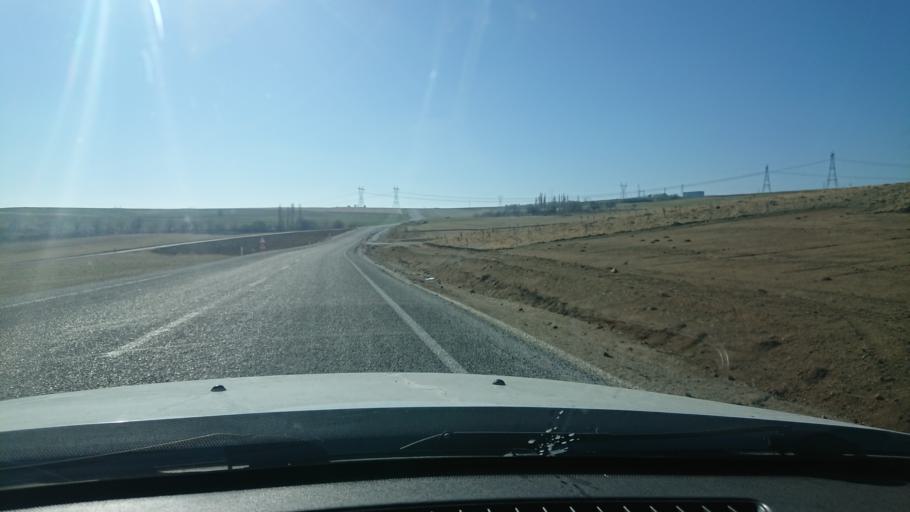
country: TR
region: Aksaray
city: Agacoren
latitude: 38.9051
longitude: 33.9342
